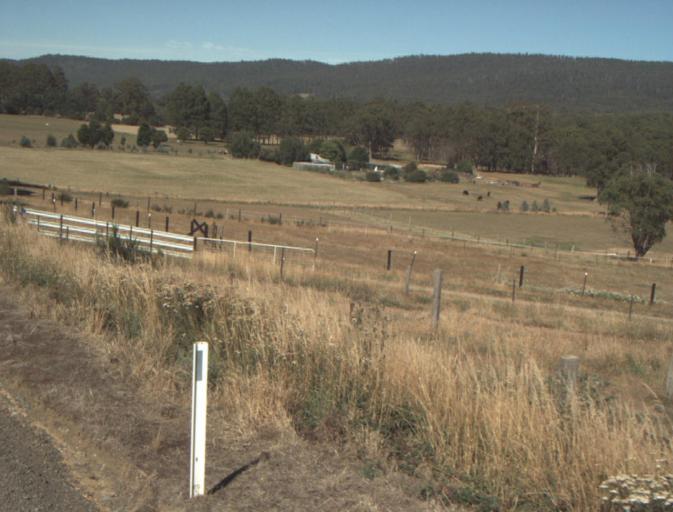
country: AU
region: Tasmania
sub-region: Launceston
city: Newstead
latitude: -41.3129
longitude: 147.3211
